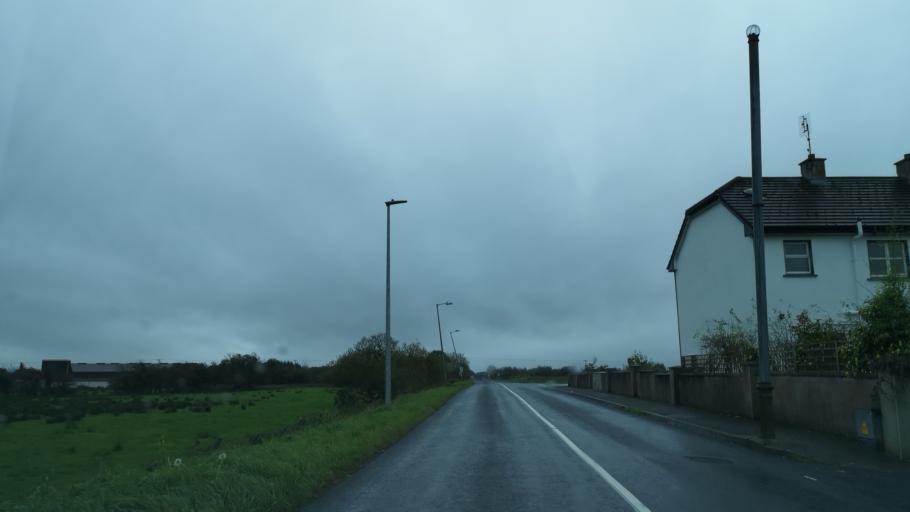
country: IE
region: Connaught
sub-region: Roscommon
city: Ballaghaderreen
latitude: 53.8992
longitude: -8.5786
